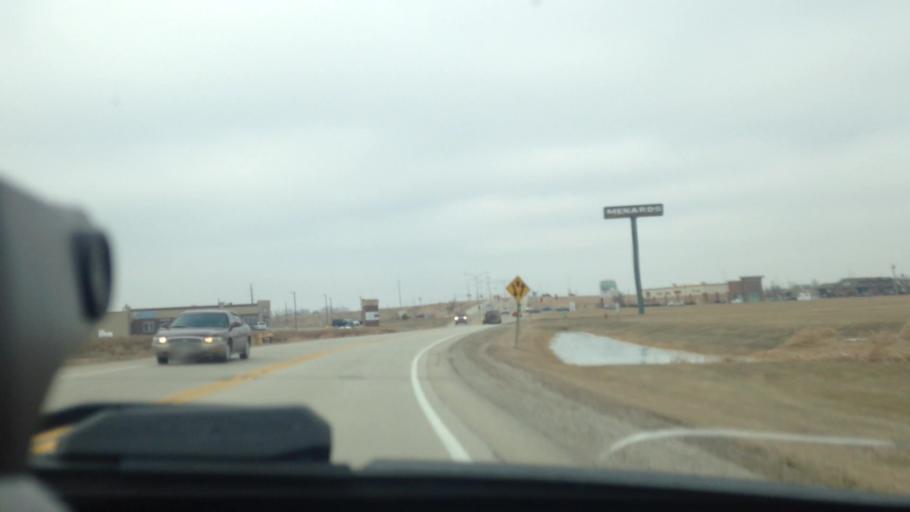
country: US
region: Wisconsin
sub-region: Dodge County
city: Beaver Dam
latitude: 43.4846
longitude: -88.8070
